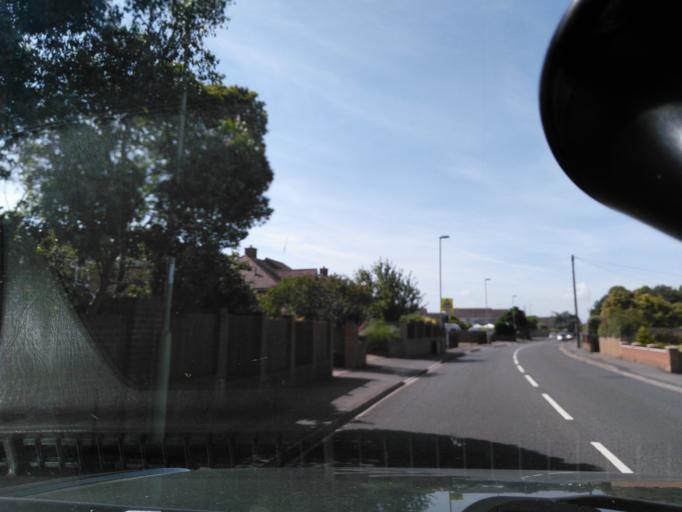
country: GB
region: England
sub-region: Hampshire
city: Lee-on-the-Solent
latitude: 50.8179
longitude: -1.2129
